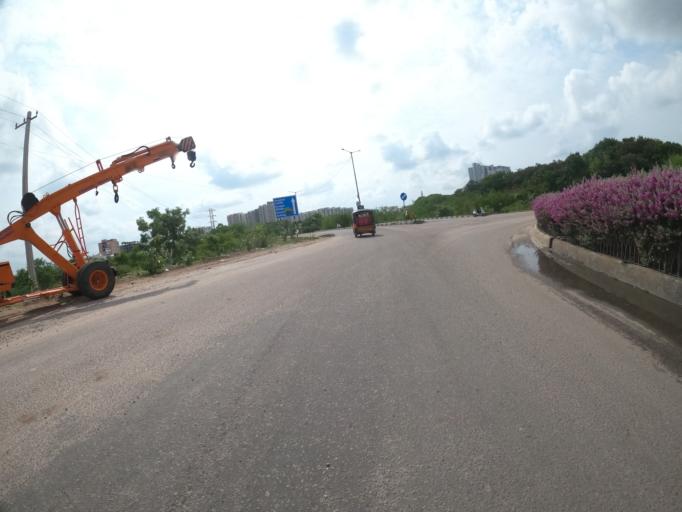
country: IN
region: Telangana
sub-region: Hyderabad
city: Hyderabad
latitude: 17.3864
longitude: 78.3473
